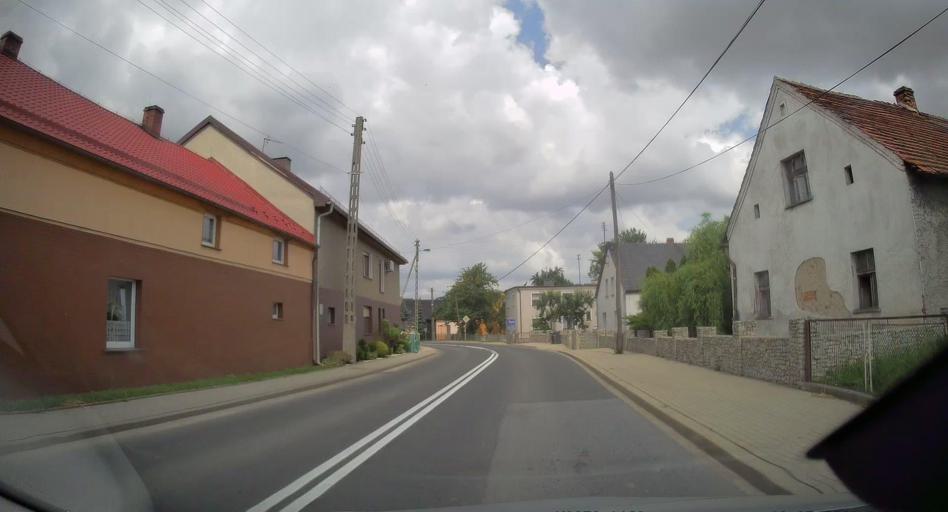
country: PL
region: Opole Voivodeship
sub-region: Powiat prudnicki
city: Twardawa
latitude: 50.3359
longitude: 17.9678
